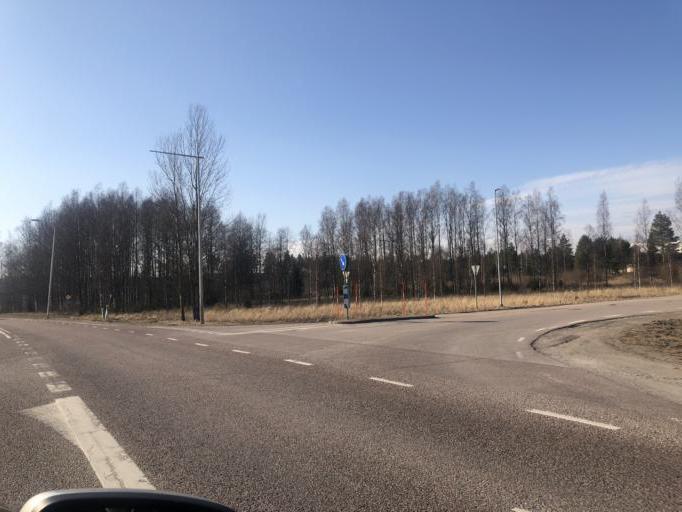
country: SE
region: Vaermland
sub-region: Filipstads Kommun
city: Filipstad
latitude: 59.7137
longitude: 14.1483
